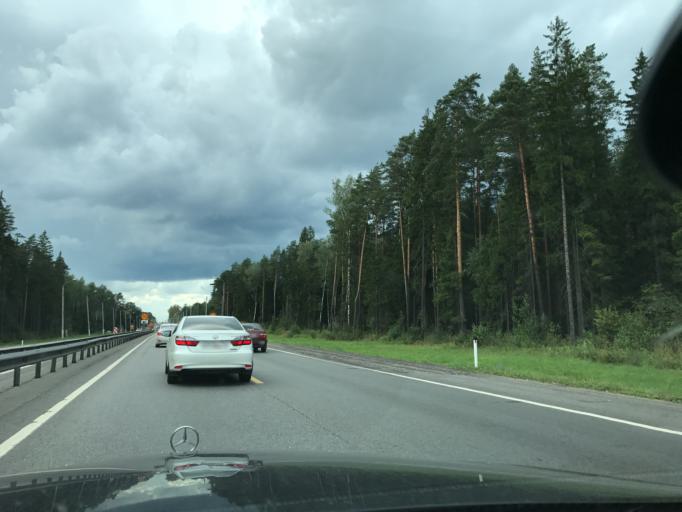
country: RU
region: Vladimir
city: Petushki
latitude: 55.9287
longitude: 39.3303
